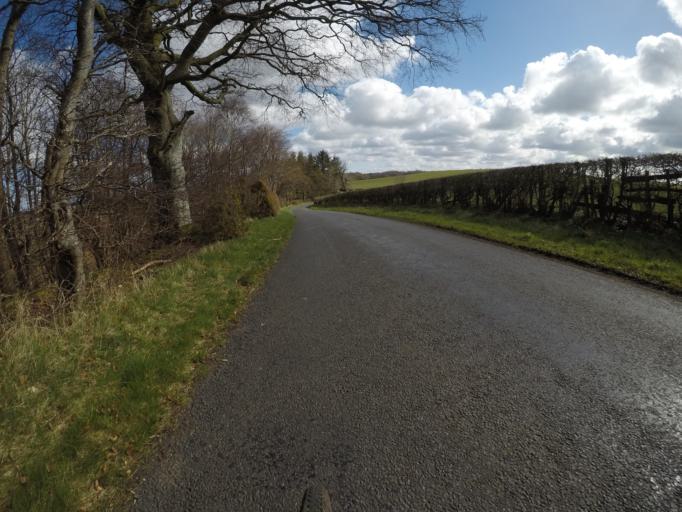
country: GB
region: Scotland
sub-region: East Ayrshire
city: Crosshouse
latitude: 55.5912
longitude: -4.5488
